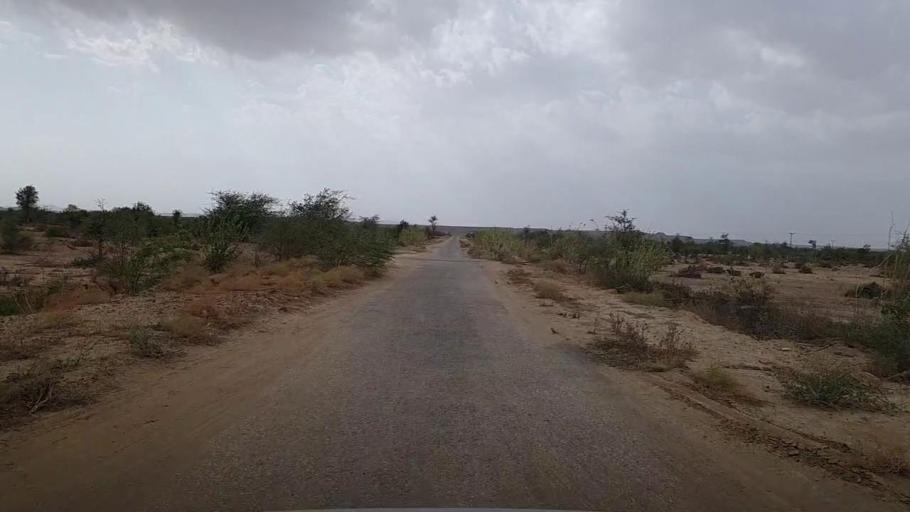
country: PK
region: Sindh
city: Jamshoro
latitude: 25.4061
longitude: 67.7061
